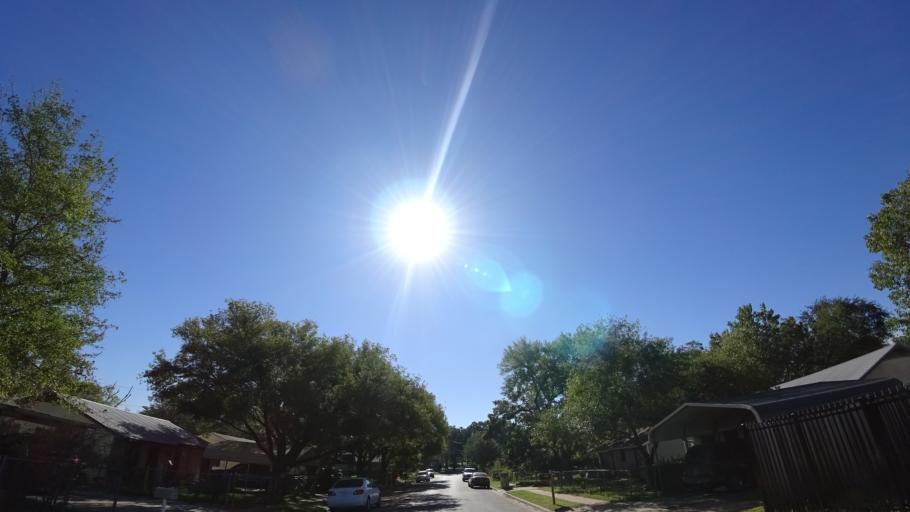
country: US
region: Texas
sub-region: Travis County
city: Austin
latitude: 30.2388
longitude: -97.6941
